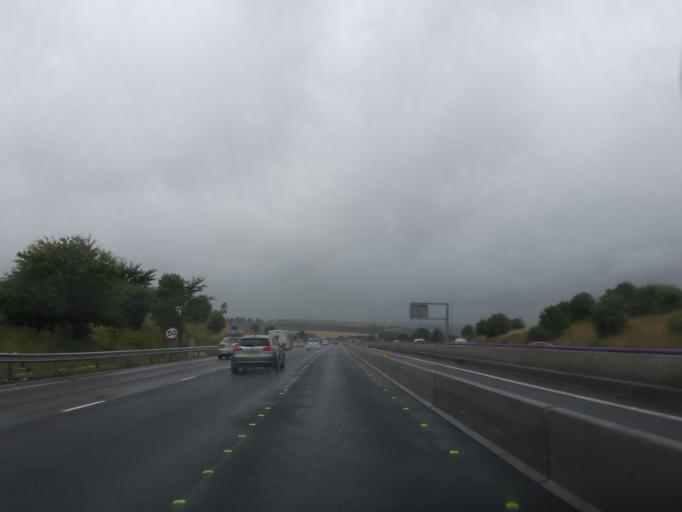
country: GB
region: England
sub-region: Derbyshire
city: Barlborough
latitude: 53.2732
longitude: -1.3025
